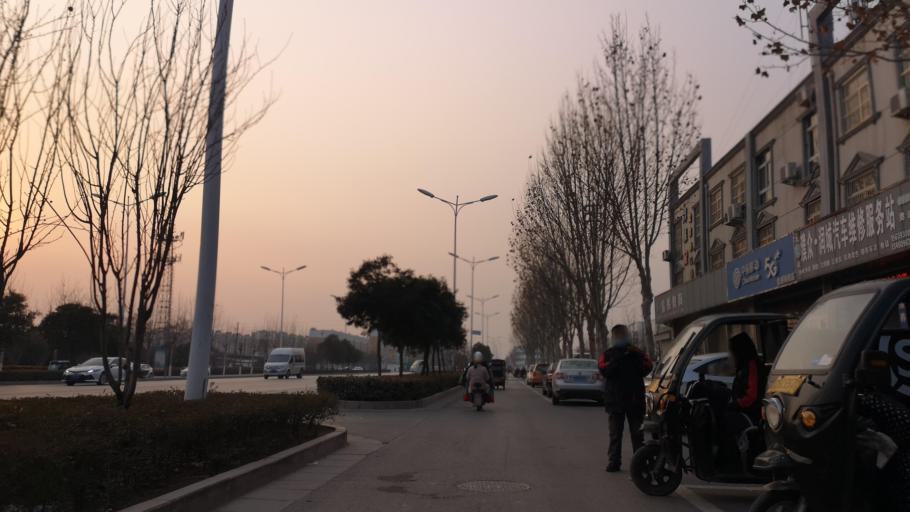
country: CN
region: Henan Sheng
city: Zhongyuanlu
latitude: 35.7890
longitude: 115.0926
